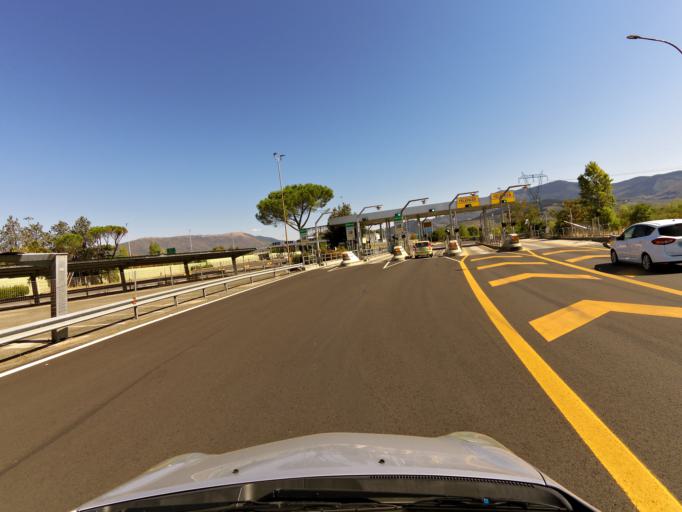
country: IT
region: Tuscany
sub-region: Province of Florence
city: Calenzano
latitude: 43.8335
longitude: 11.1610
